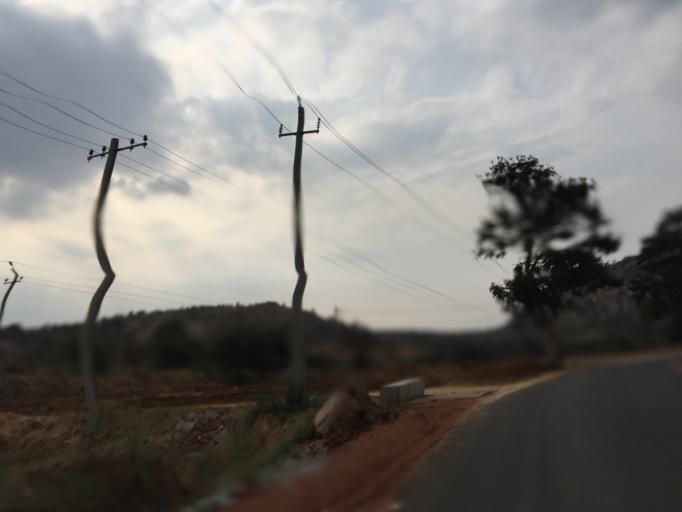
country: IN
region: Karnataka
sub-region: Chikkaballapur
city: Gudibanda
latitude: 13.5579
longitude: 77.7384
